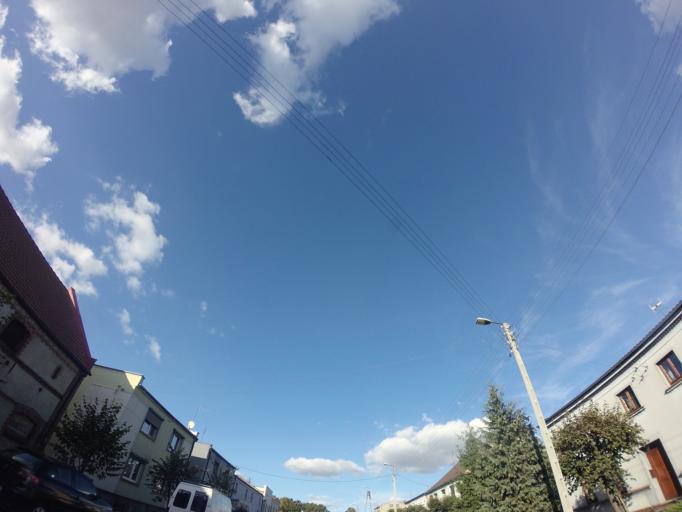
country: PL
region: Greater Poland Voivodeship
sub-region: Powiat grodziski
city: Rakoniewice
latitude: 52.1396
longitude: 16.2753
